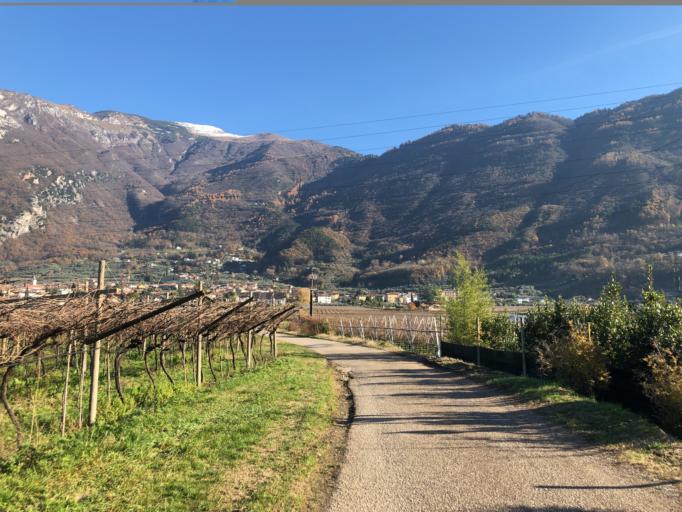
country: IT
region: Trentino-Alto Adige
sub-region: Provincia di Trento
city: Arco
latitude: 45.9097
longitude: 10.8929
